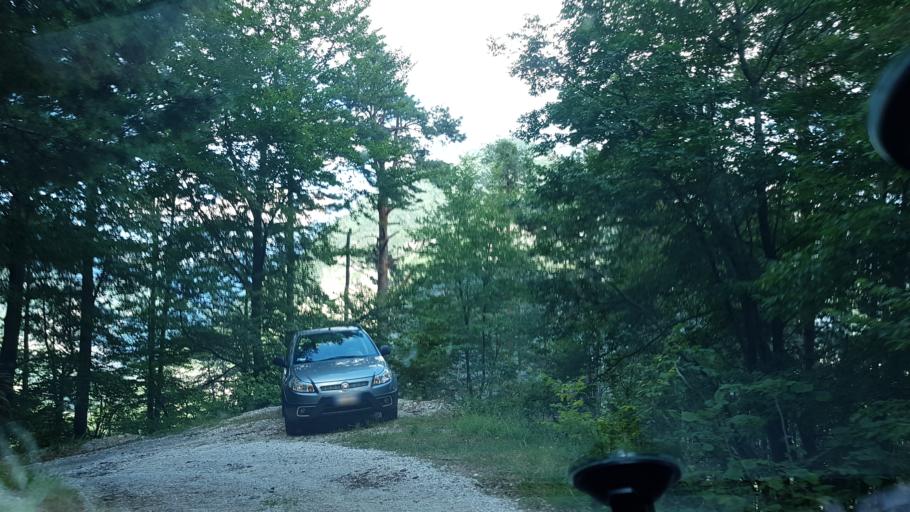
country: IT
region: Friuli Venezia Giulia
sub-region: Provincia di Udine
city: Dogna
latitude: 46.4418
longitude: 13.2984
